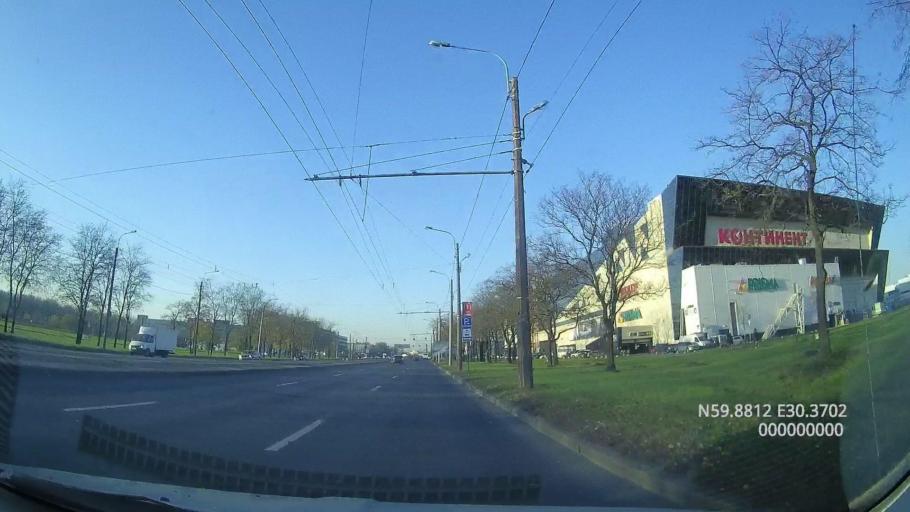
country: RU
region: St.-Petersburg
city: Kupchino
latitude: 59.8812
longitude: 30.3707
